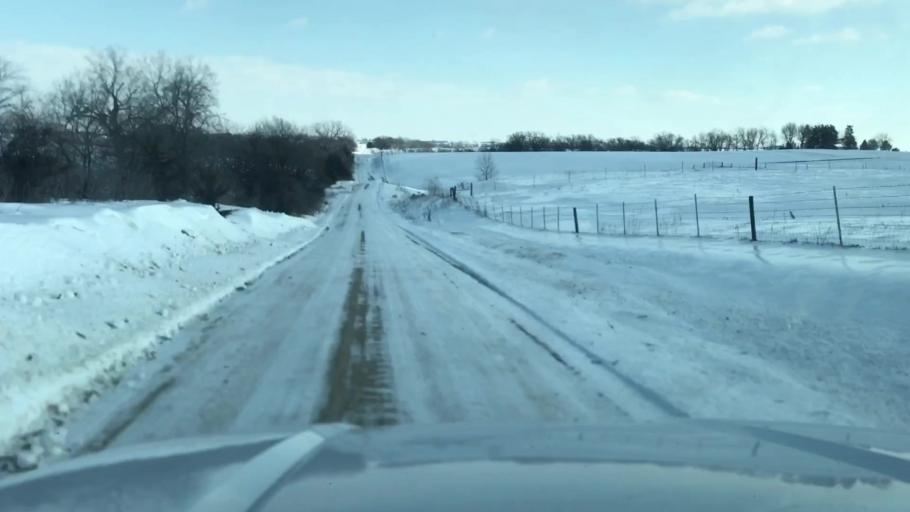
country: US
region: Missouri
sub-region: Nodaway County
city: Maryville
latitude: 40.3867
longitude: -94.7086
